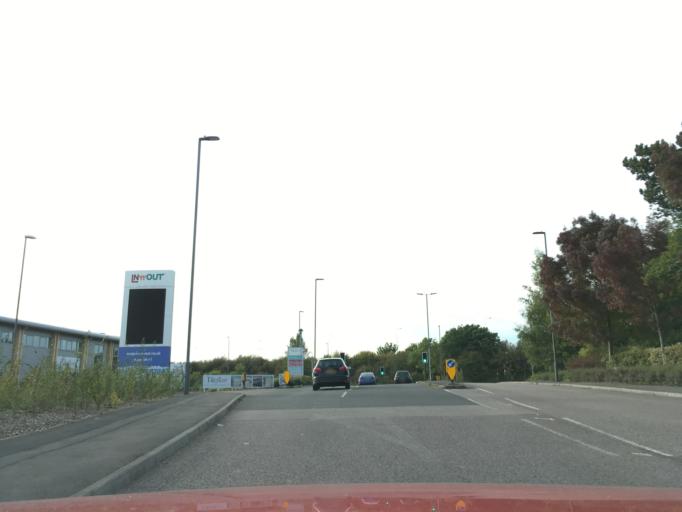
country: GB
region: England
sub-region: South Gloucestershire
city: Almondsbury
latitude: 51.5280
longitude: -2.6056
